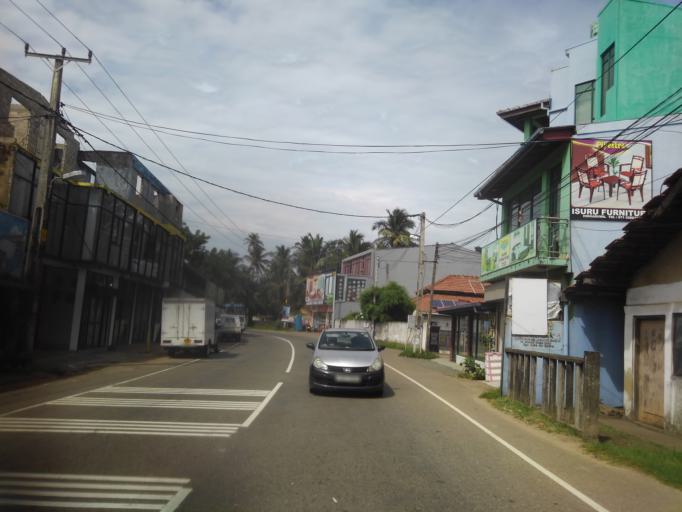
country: LK
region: Southern
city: Hikkaduwa
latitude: 6.1432
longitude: 80.0999
